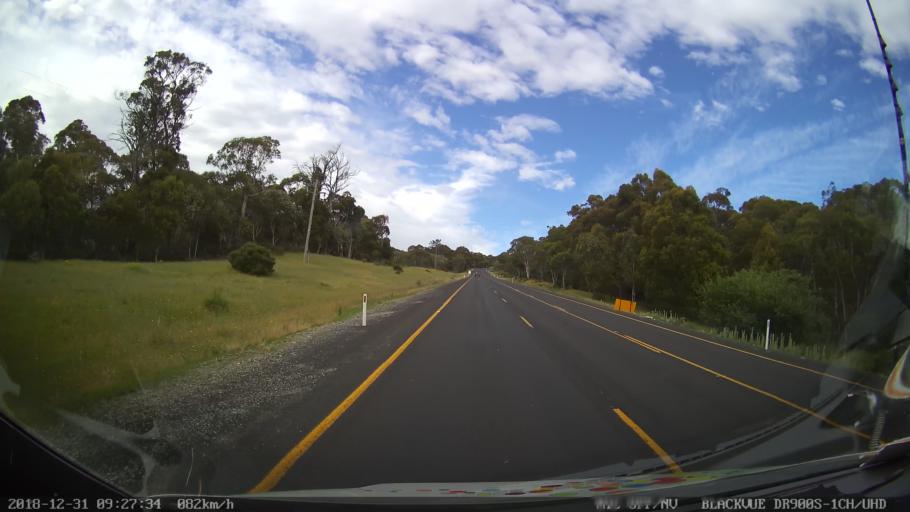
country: AU
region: New South Wales
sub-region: Snowy River
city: Jindabyne
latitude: -36.4570
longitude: 148.4831
